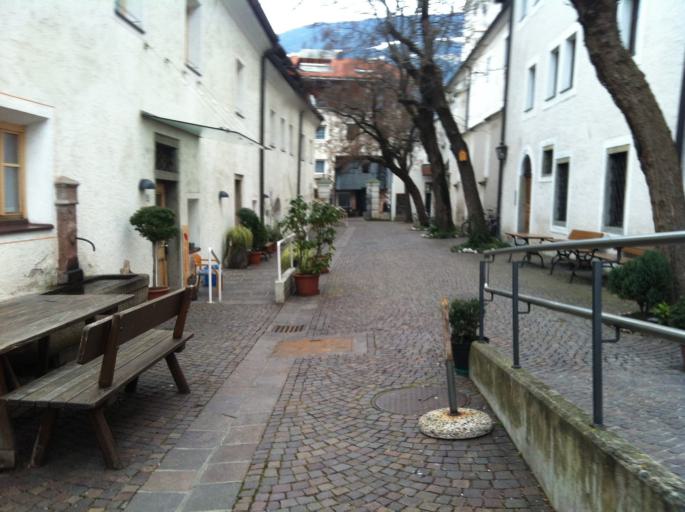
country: IT
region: Trentino-Alto Adige
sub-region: Bolzano
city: Bressanone
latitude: 46.7172
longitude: 11.6542
